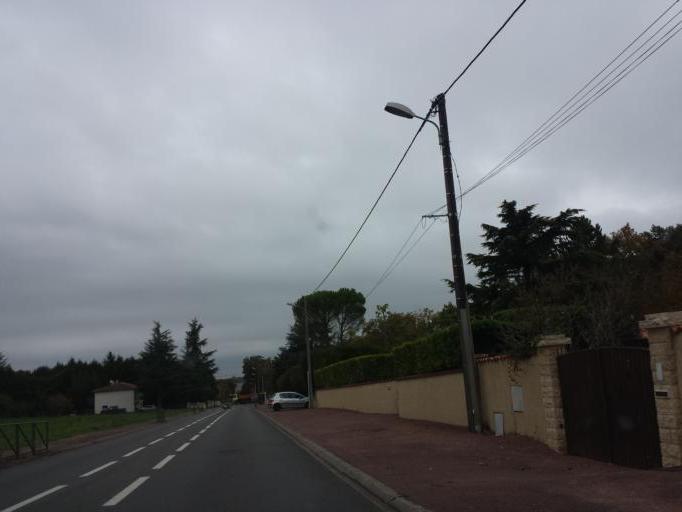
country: FR
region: Poitou-Charentes
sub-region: Departement de la Charente
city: Puymoyen
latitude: 45.6186
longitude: 0.1719
